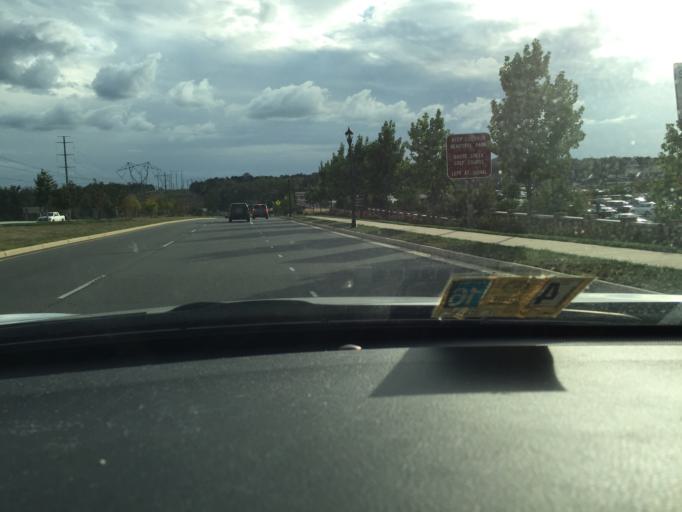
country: US
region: Virginia
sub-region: Loudoun County
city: Belmont
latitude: 39.0888
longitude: -77.5198
